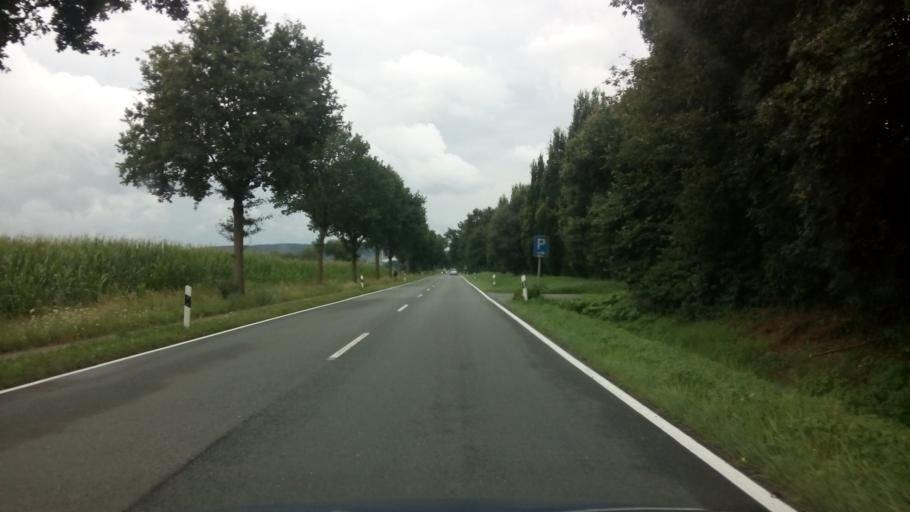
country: DE
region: Lower Saxony
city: Bohmte
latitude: 52.3516
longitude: 8.3142
